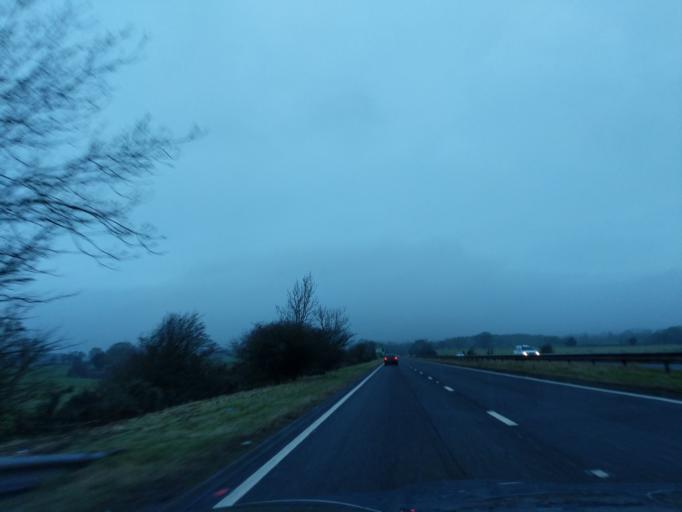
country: GB
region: England
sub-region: Northumberland
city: Morpeth
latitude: 55.1556
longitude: -1.7155
